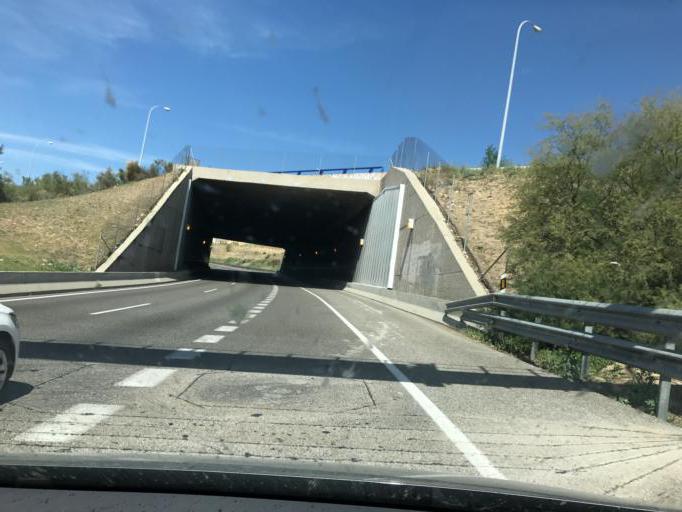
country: ES
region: Madrid
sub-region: Provincia de Madrid
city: Leganes
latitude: 40.3581
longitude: -3.7600
